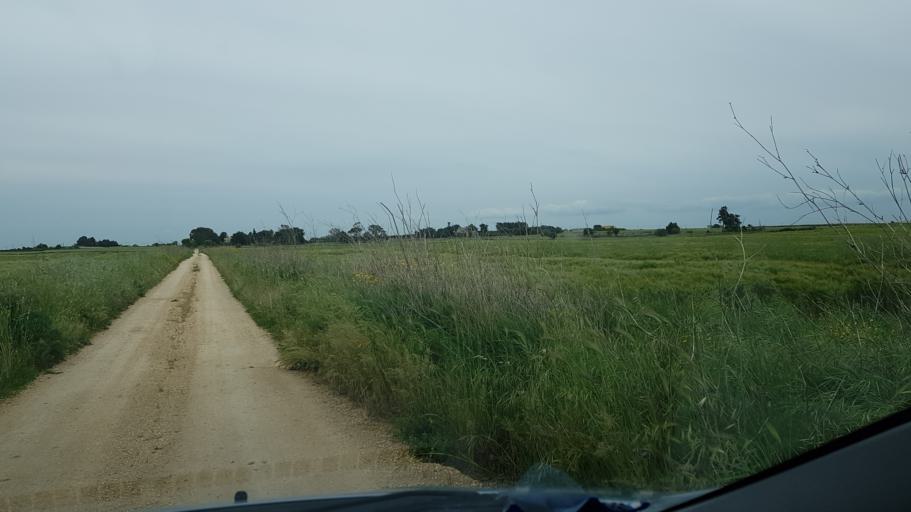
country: IT
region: Apulia
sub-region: Provincia di Brindisi
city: Brindisi
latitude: 40.6546
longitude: 17.8819
